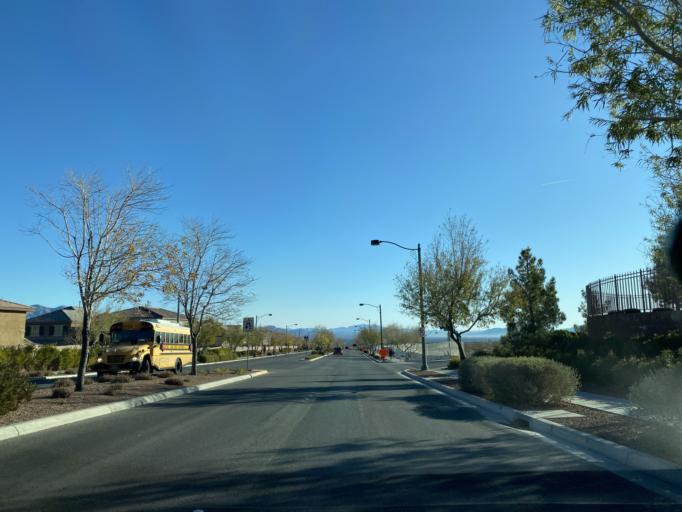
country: US
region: Nevada
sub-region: Clark County
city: Summerlin South
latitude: 36.2991
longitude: -115.3271
